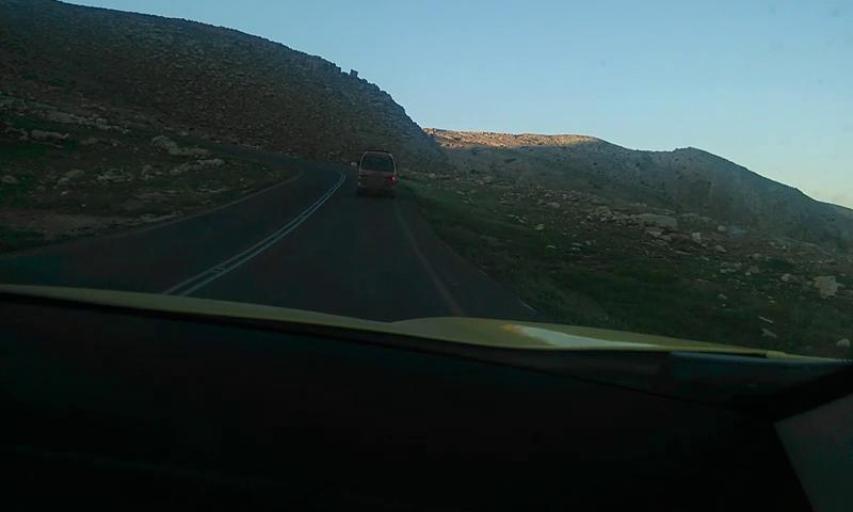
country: PS
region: West Bank
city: Rammun
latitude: 31.9143
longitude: 35.3570
